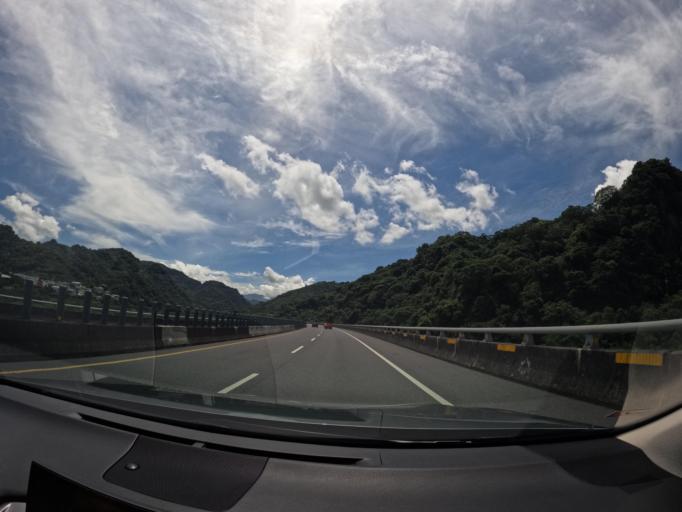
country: TW
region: Taiwan
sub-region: Miaoli
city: Miaoli
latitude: 24.4639
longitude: 120.8292
